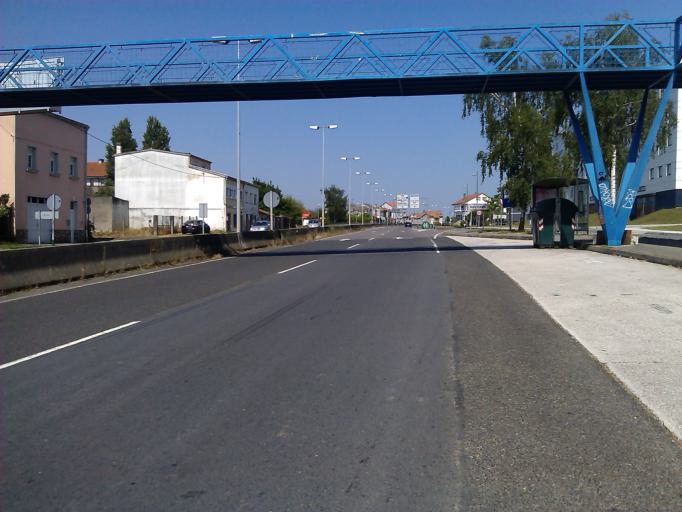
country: ES
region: Galicia
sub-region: Provincia da Coruna
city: Santiago de Compostela
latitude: 42.8579
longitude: -8.5347
